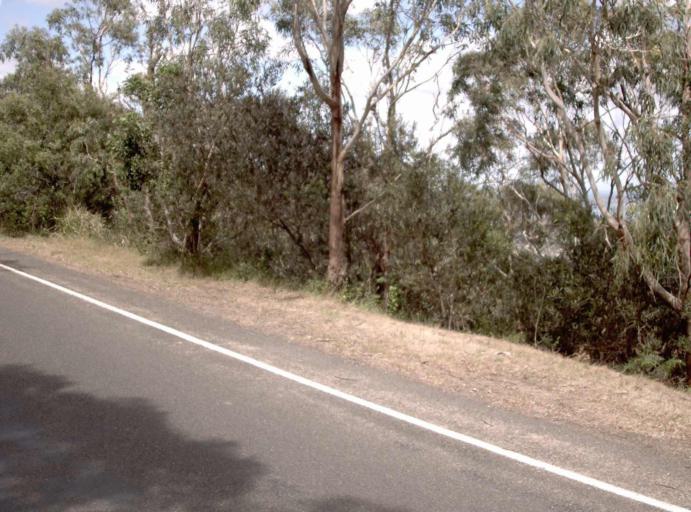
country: AU
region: Victoria
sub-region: Mornington Peninsula
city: McCrae
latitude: -38.3524
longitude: 144.9490
